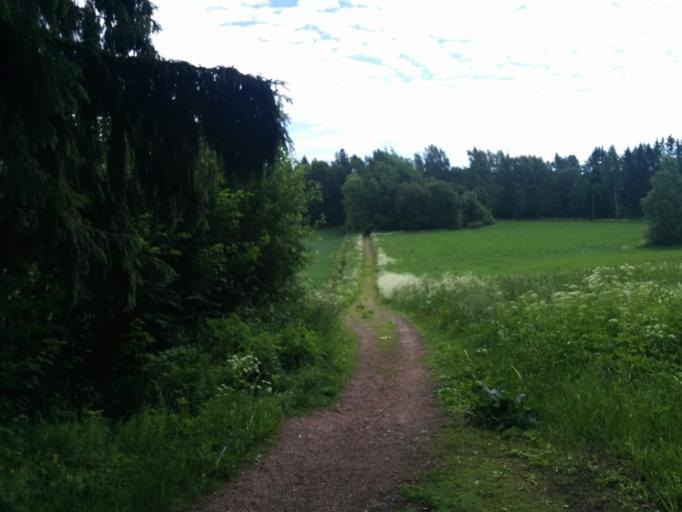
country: FI
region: Uusimaa
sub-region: Helsinki
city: Vantaa
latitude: 60.2379
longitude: 25.1297
